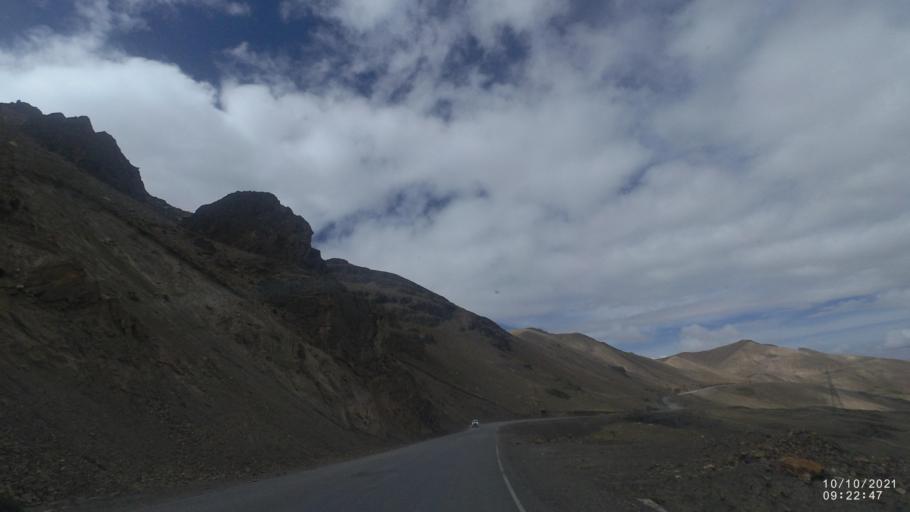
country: BO
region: La Paz
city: Quime
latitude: -17.0802
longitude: -67.2991
